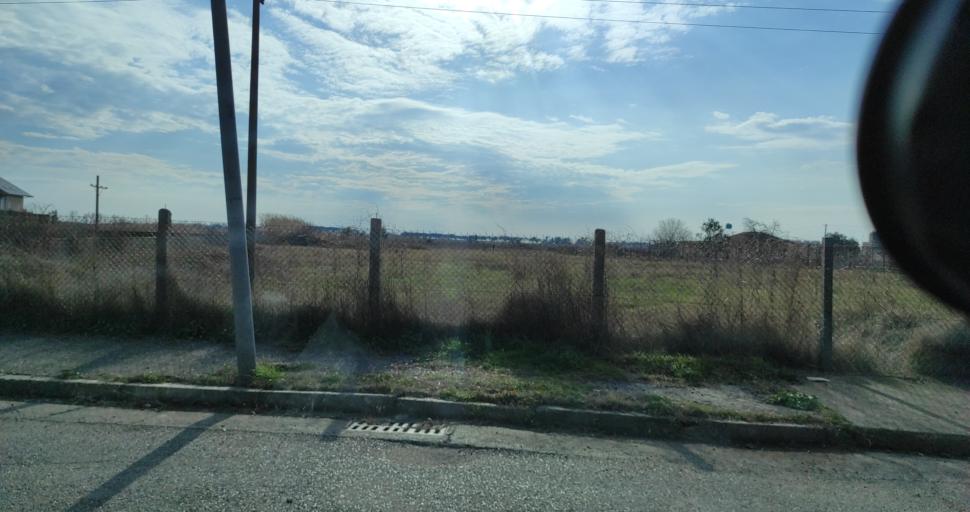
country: AL
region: Lezhe
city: Lezhe
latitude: 41.7954
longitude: 19.6206
